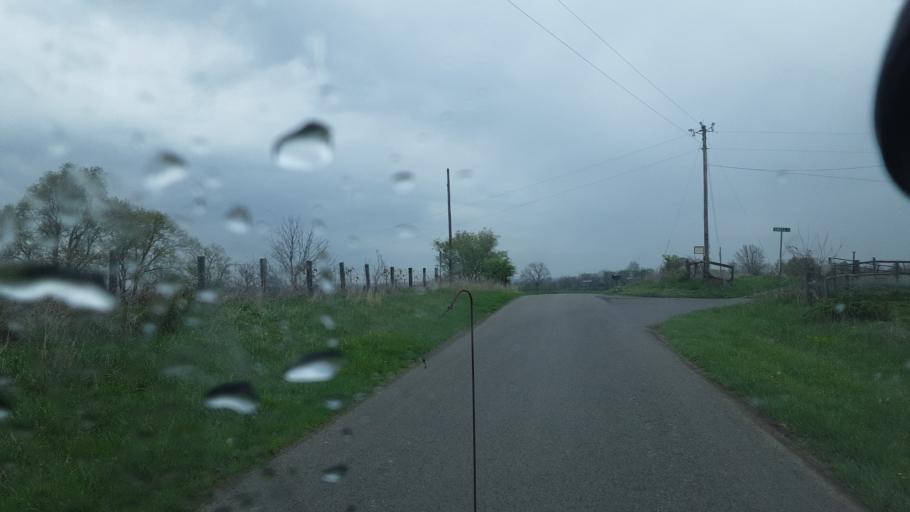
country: US
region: Kentucky
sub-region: Owen County
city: Owenton
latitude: 38.6109
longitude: -84.7712
